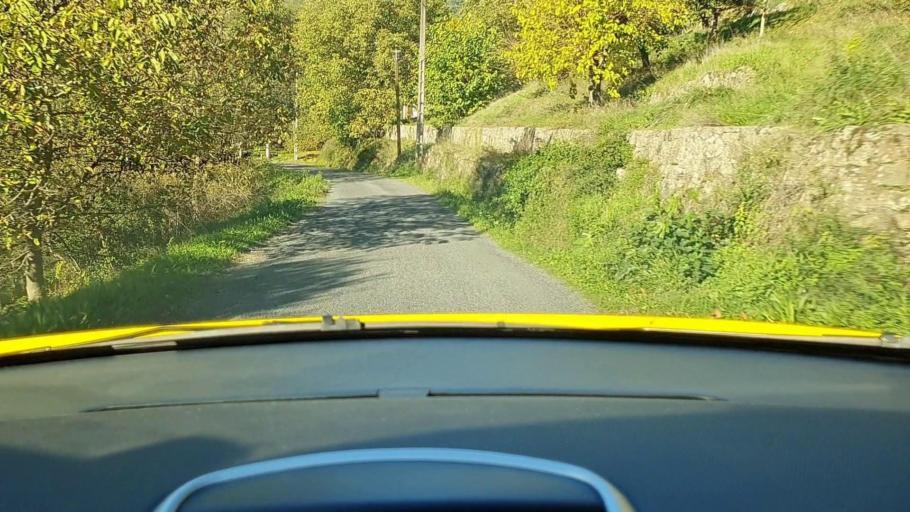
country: FR
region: Languedoc-Roussillon
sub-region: Departement du Gard
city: Valleraugue
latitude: 44.0371
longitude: 3.6807
